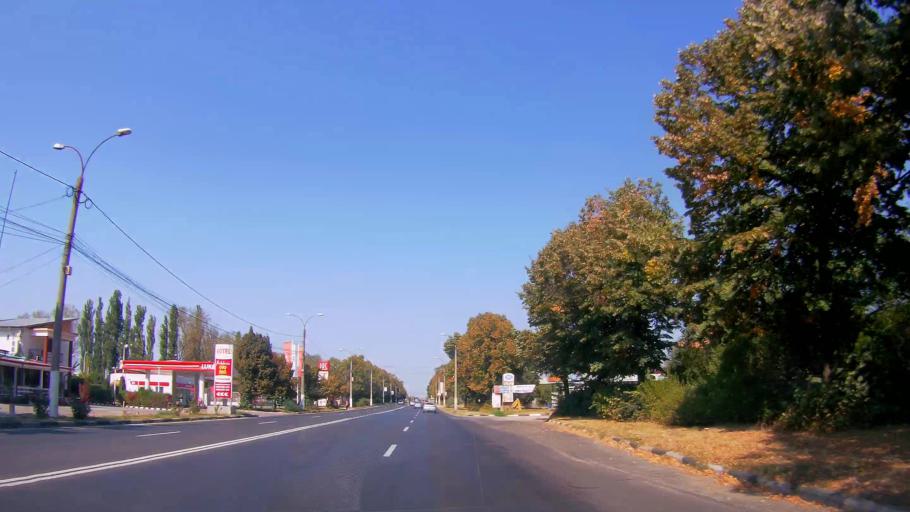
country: RO
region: Giurgiu
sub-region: Comuna Fratesti
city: Remus
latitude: 43.9276
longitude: 25.9750
